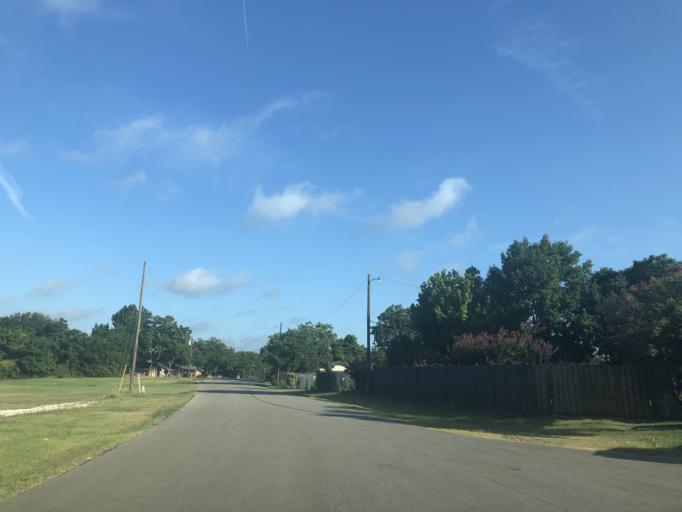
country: US
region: Texas
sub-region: Dallas County
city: Duncanville
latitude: 32.6683
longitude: -96.9099
